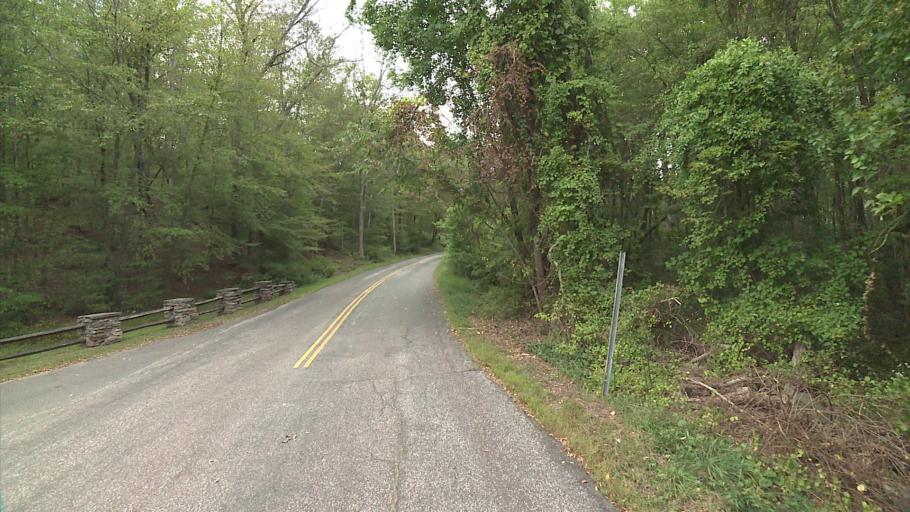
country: US
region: Connecticut
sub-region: Middlesex County
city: Higganum
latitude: 41.5232
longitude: -72.5320
